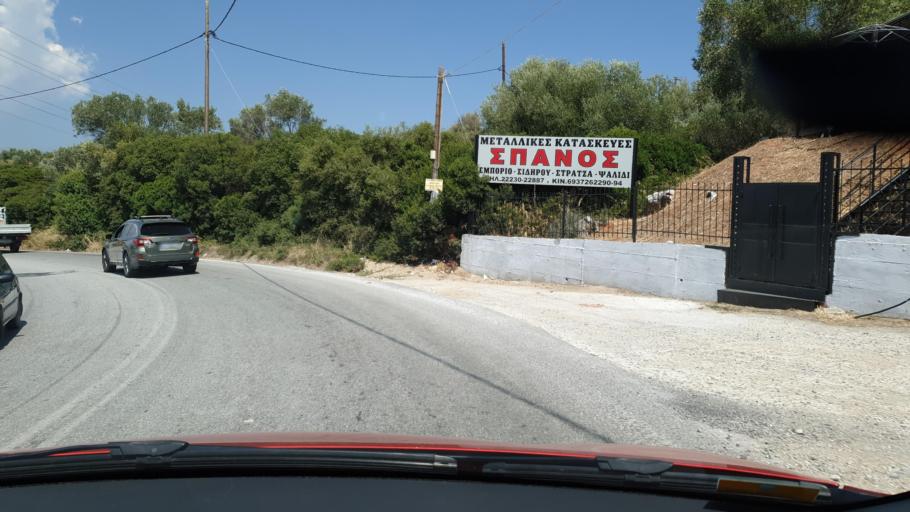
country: GR
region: Central Greece
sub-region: Nomos Evvoias
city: Aliveri
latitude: 38.3962
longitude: 24.0650
